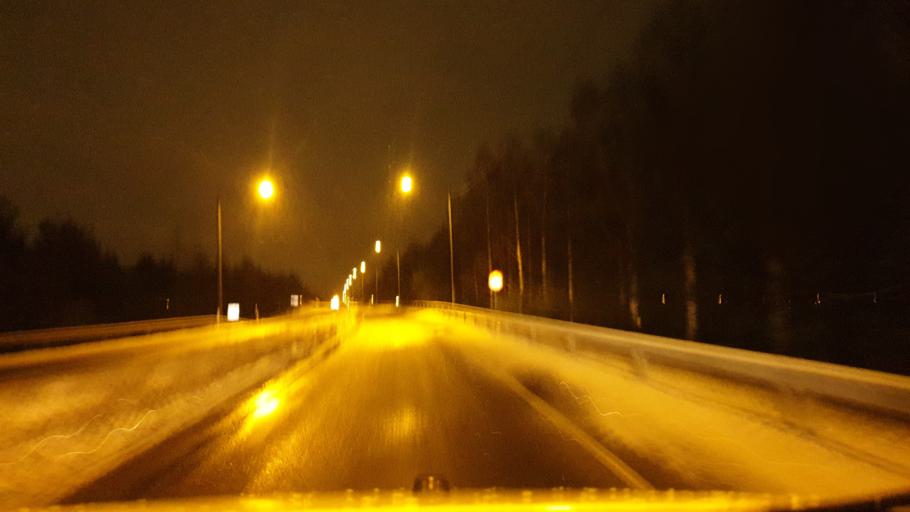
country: FI
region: Northern Ostrobothnia
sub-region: Oulu
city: Oulu
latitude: 64.9839
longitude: 25.4735
